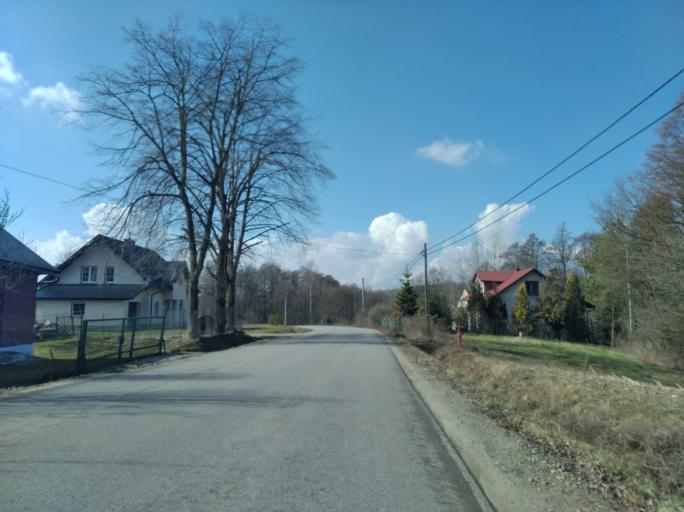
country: PL
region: Subcarpathian Voivodeship
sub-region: Powiat debicki
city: Brzostek
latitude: 49.8873
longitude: 21.4668
